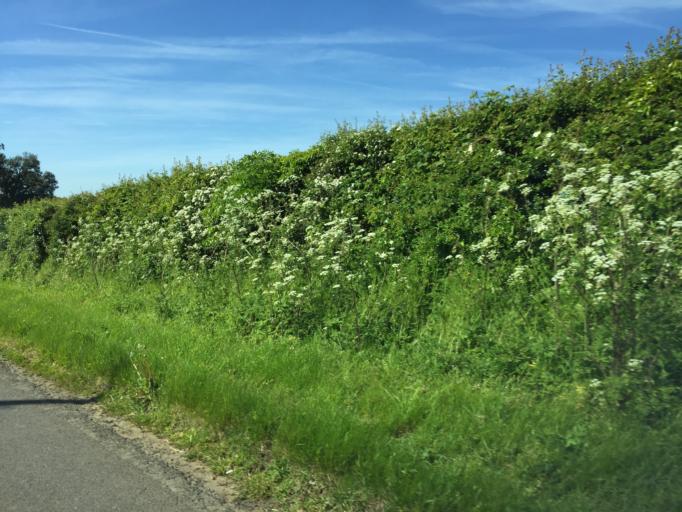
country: GB
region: England
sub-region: South Gloucestershire
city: Horton
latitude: 51.5300
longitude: -2.3091
